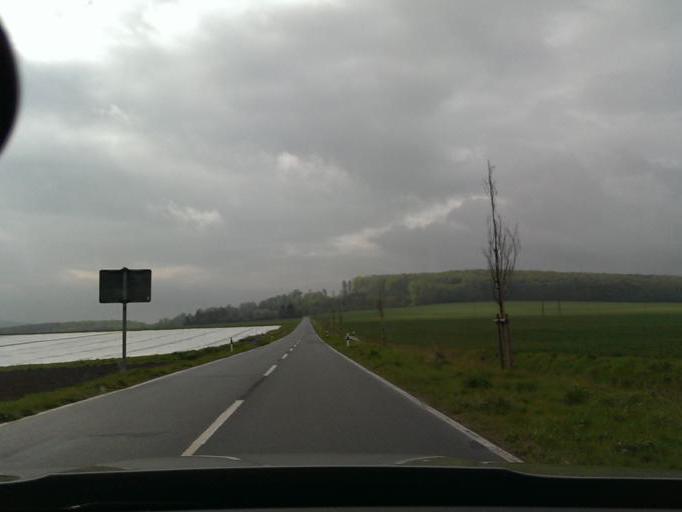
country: DE
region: Lower Saxony
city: Nordstemmen
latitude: 52.1863
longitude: 9.7617
